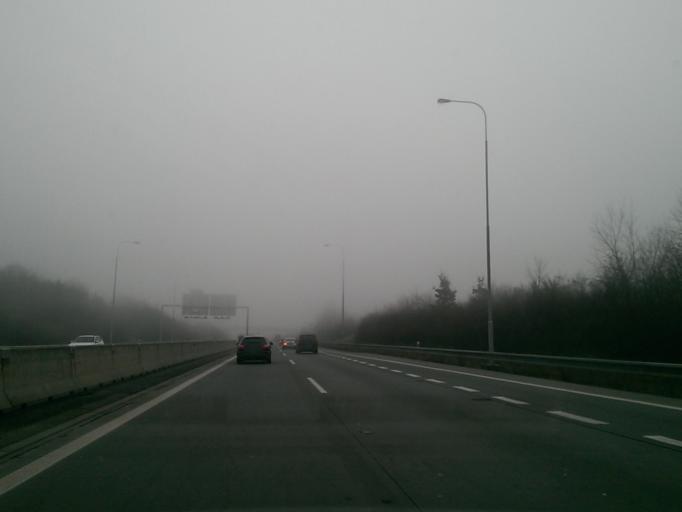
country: CZ
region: Olomoucky
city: Hnevotin
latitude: 49.5622
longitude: 17.2211
